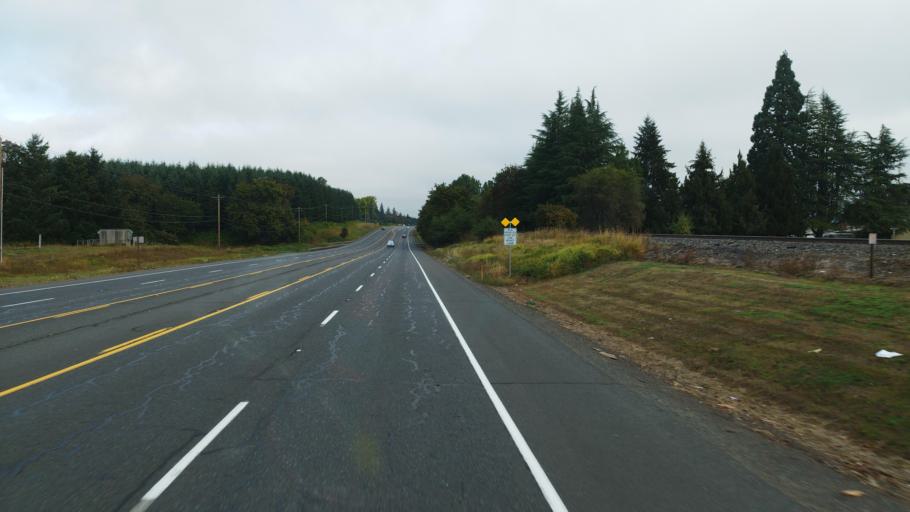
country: US
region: Oregon
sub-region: Columbia County
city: Scappoose
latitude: 45.7870
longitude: -122.8717
